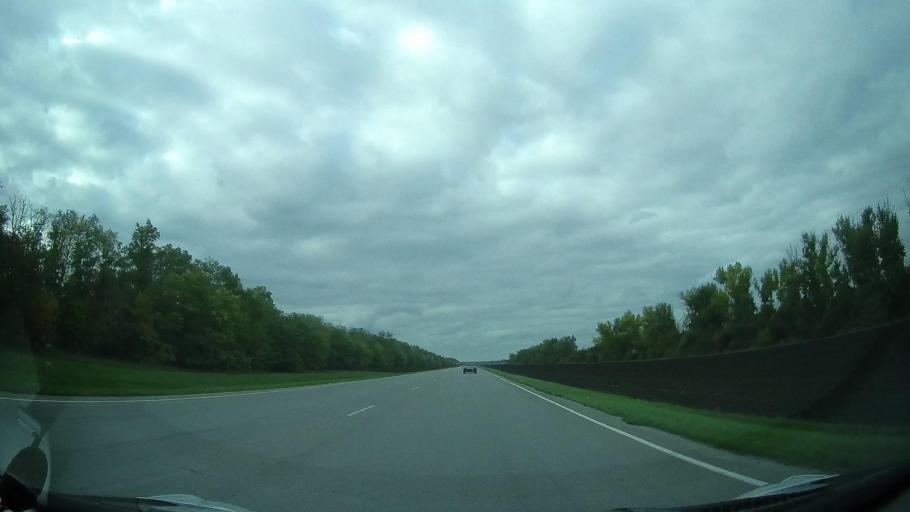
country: RU
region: Rostov
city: Yegorlykskaya
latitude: 46.6386
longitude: 40.5810
